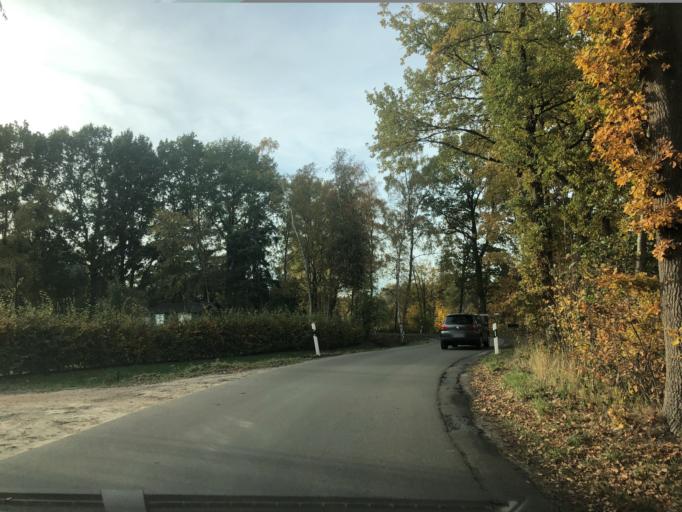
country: DE
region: Lower Saxony
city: Edewecht
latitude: 53.0891
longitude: 8.0311
